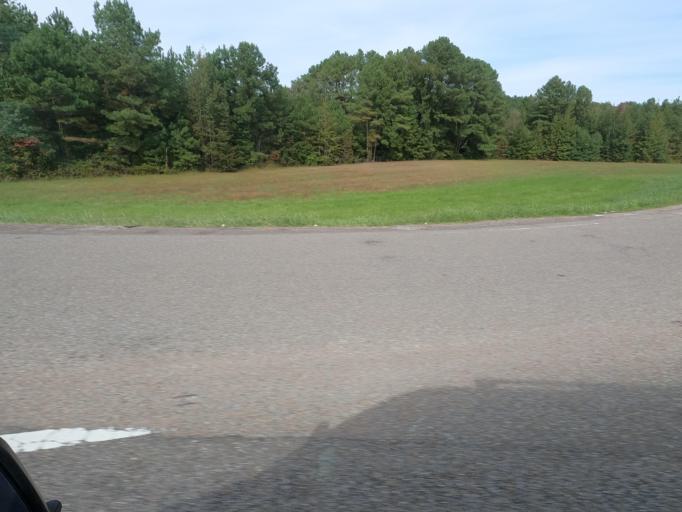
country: US
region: Tennessee
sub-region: Henderson County
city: Lexington
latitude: 35.7599
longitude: -88.4911
